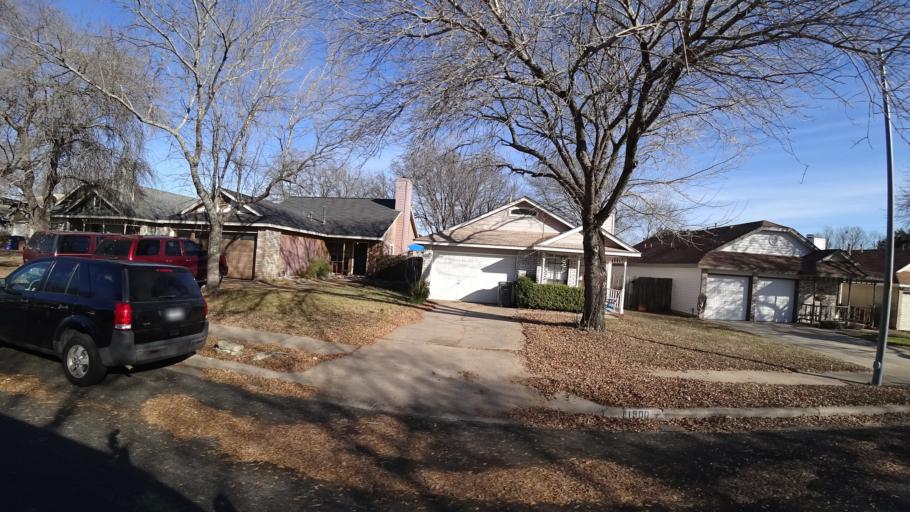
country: US
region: Texas
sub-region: Travis County
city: Wells Branch
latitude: 30.3963
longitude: -97.7030
